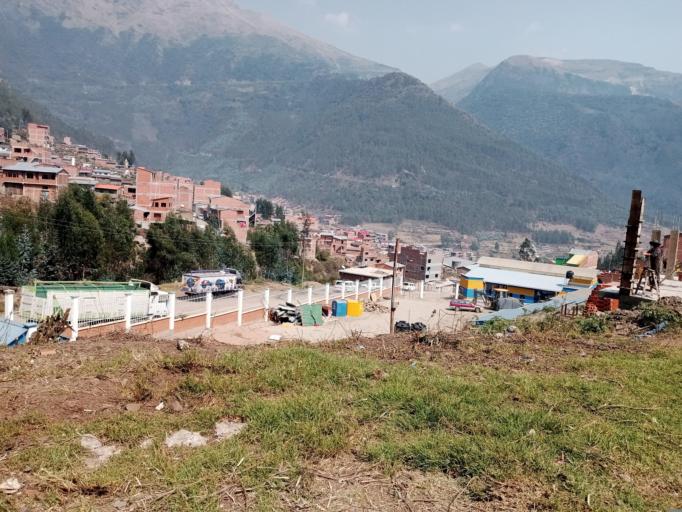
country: BO
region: La Paz
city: Quime
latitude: -16.9839
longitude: -67.2138
